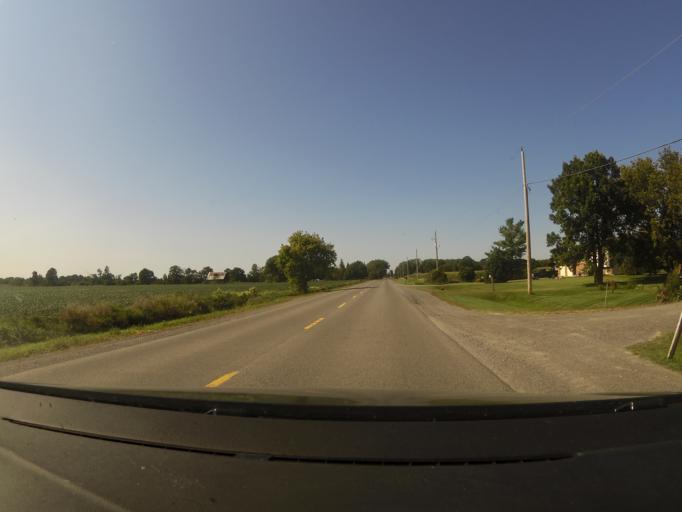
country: CA
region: Ontario
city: Carleton Place
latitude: 45.3436
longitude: -76.0807
